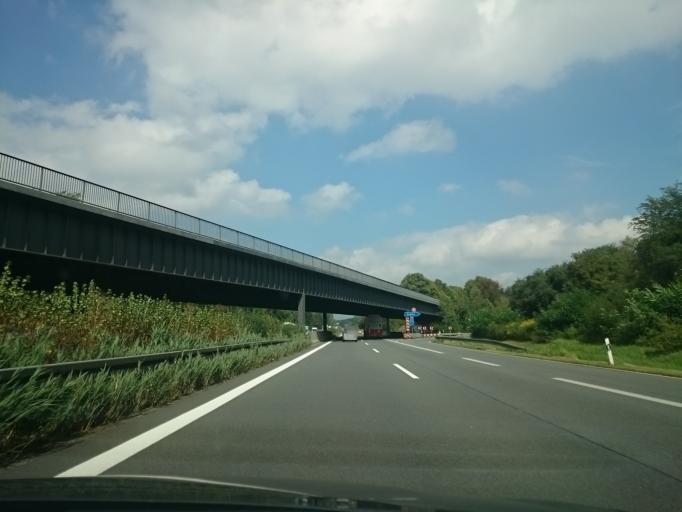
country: DE
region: Brandenburg
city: Bernau bei Berlin
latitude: 52.6489
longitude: 13.5681
